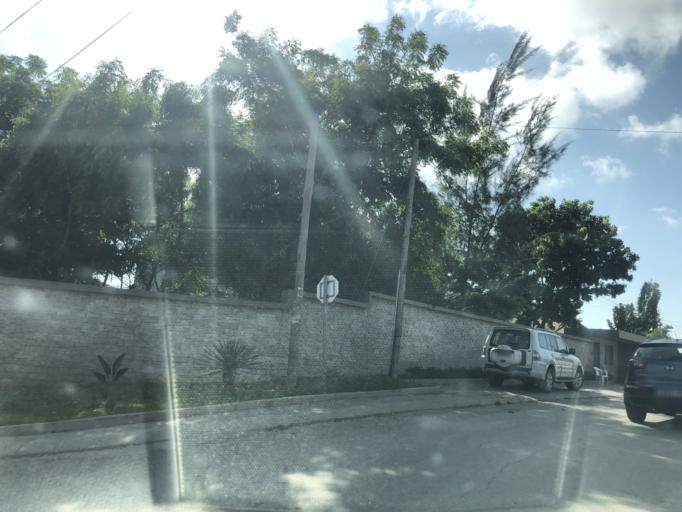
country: AO
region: Luanda
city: Luanda
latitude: -8.9081
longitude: 13.2296
